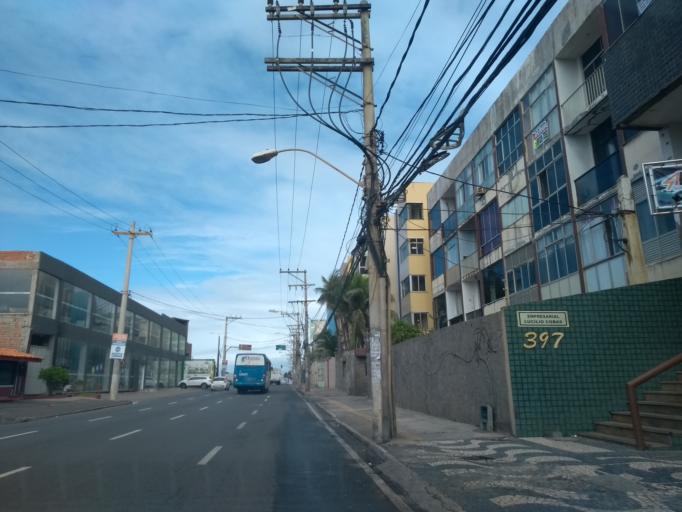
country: BR
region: Bahia
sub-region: Salvador
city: Salvador
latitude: -13.0003
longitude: -38.4505
